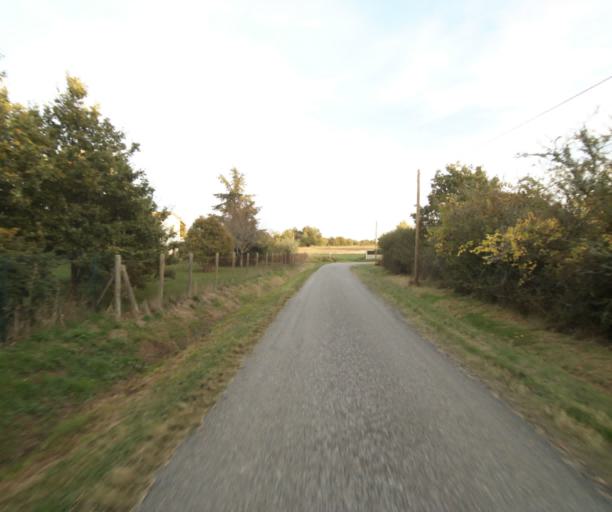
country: FR
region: Midi-Pyrenees
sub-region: Departement du Tarn-et-Garonne
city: Pompignan
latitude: 43.8307
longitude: 1.3111
